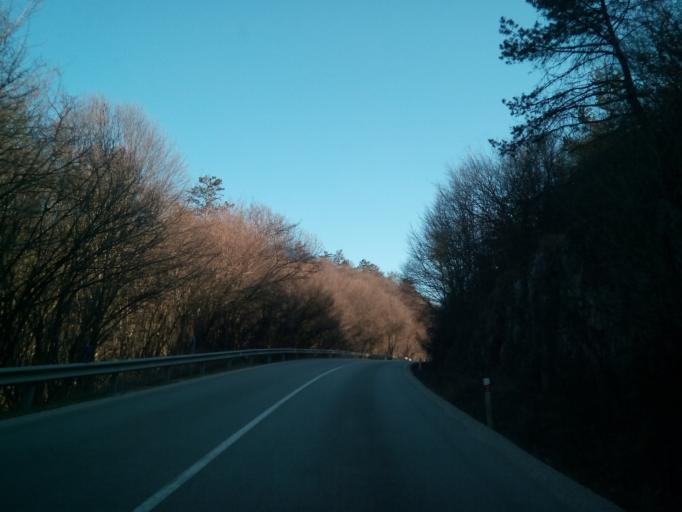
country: SK
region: Kosicky
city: Roznava
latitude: 48.6055
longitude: 20.6375
